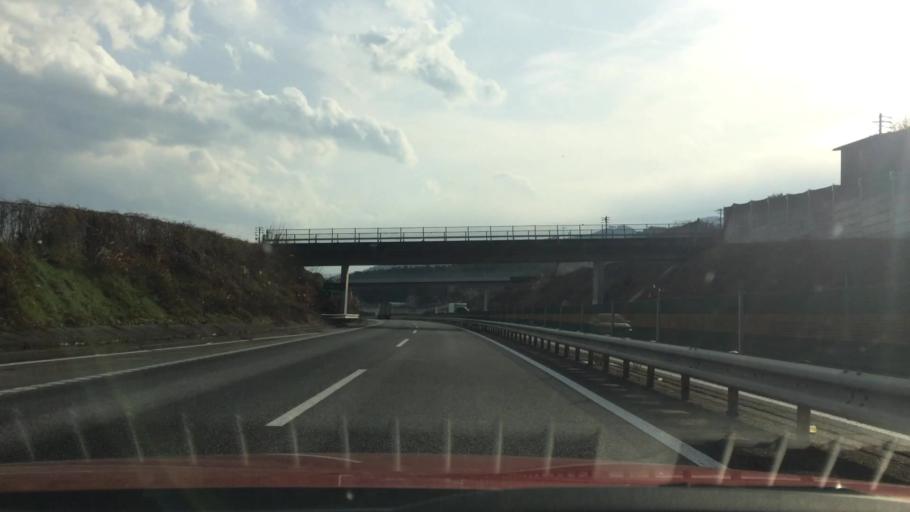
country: JP
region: Nagano
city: Ina
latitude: 35.8173
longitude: 137.9258
